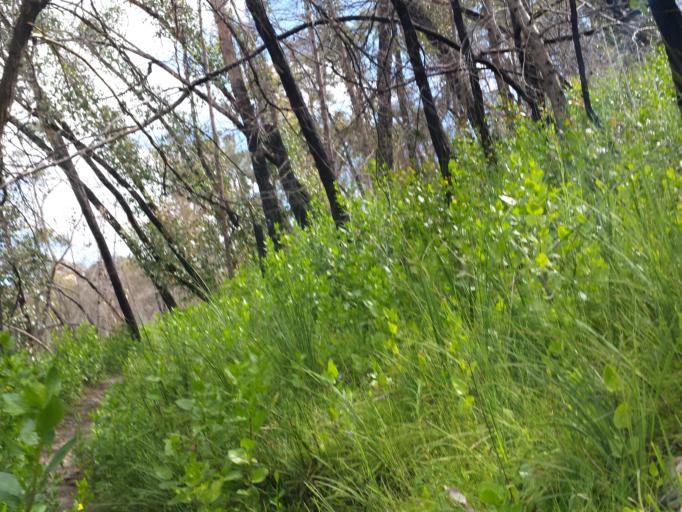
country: AU
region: Victoria
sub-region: Northern Grampians
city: Stawell
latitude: -37.2478
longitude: 142.2788
